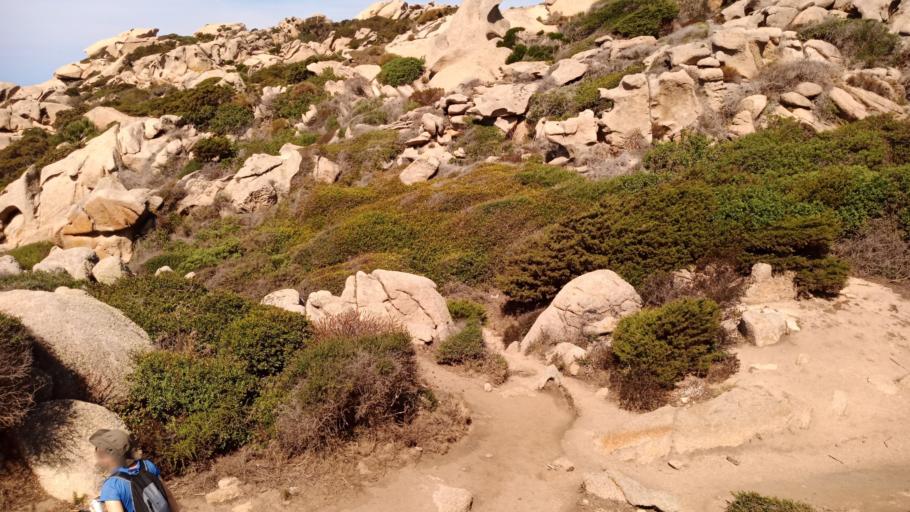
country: IT
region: Sardinia
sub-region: Provincia di Olbia-Tempio
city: Santa Teresa Gallura
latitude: 41.2381
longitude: 9.1467
